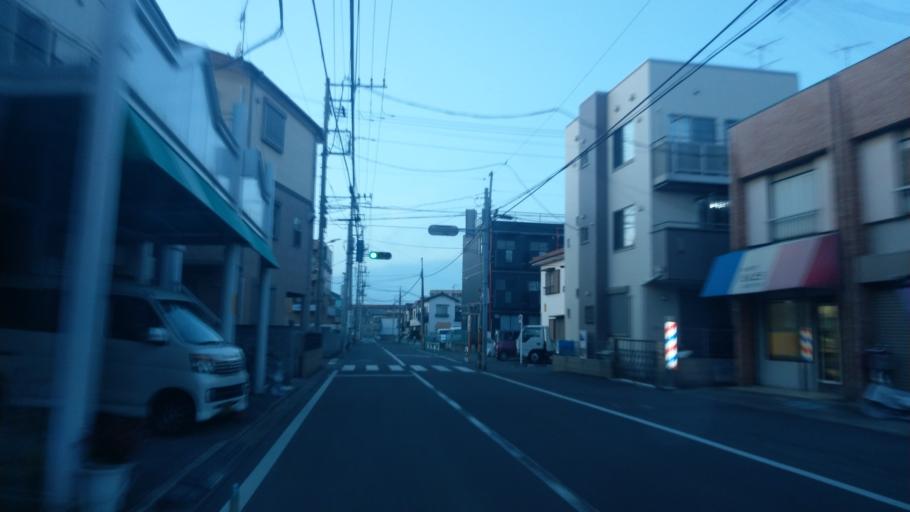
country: JP
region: Saitama
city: Yono
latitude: 35.8757
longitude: 139.6044
